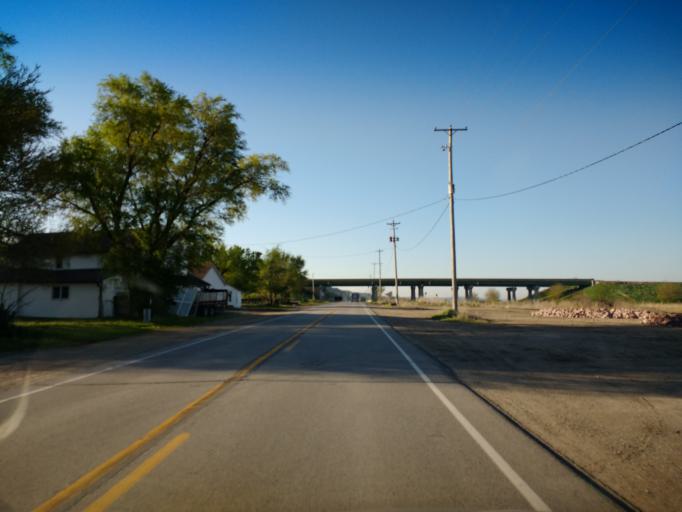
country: US
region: Iowa
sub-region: Harrison County
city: Missouri Valley
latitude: 41.4968
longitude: -95.8922
